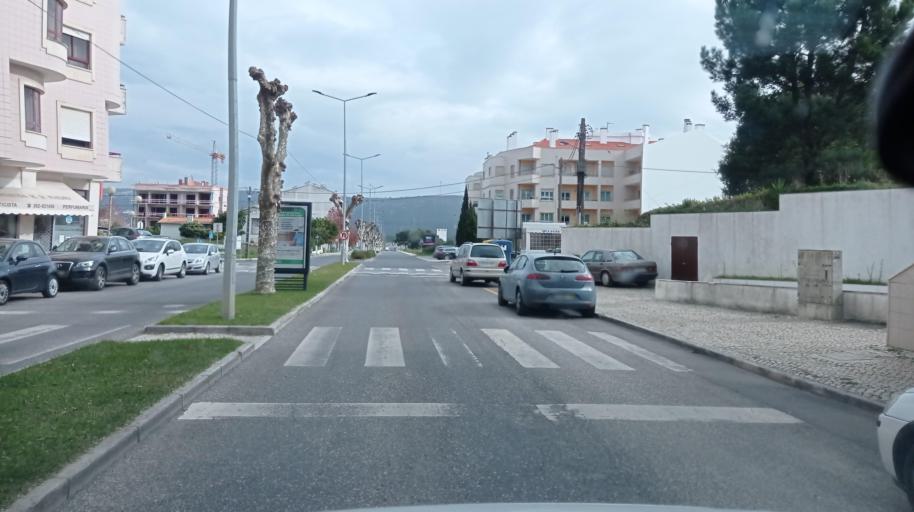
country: PT
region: Leiria
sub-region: Alcobaca
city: Benedita
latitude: 39.4257
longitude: -8.9795
